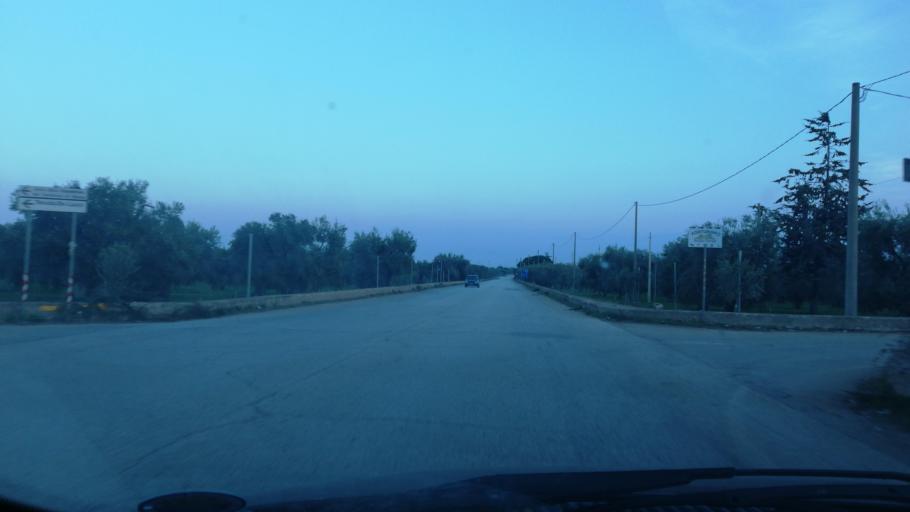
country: IT
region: Apulia
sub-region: Provincia di Bari
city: Bitonto
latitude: 41.1308
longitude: 16.7076
